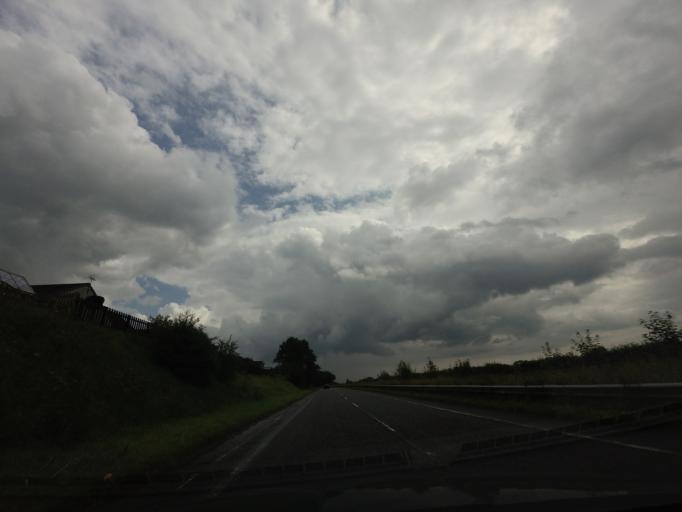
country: GB
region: Scotland
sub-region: Dumfries and Galloway
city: Lockerbie
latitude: 55.1134
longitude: -3.3573
